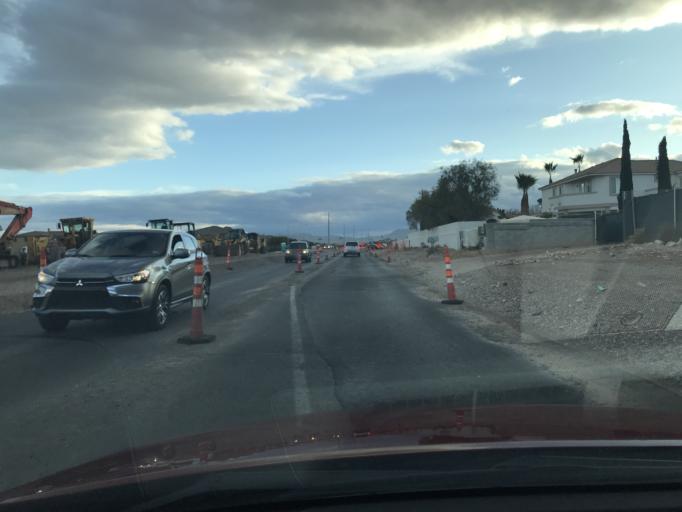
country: US
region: Nevada
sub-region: Clark County
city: Enterprise
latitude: 36.0311
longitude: -115.2789
